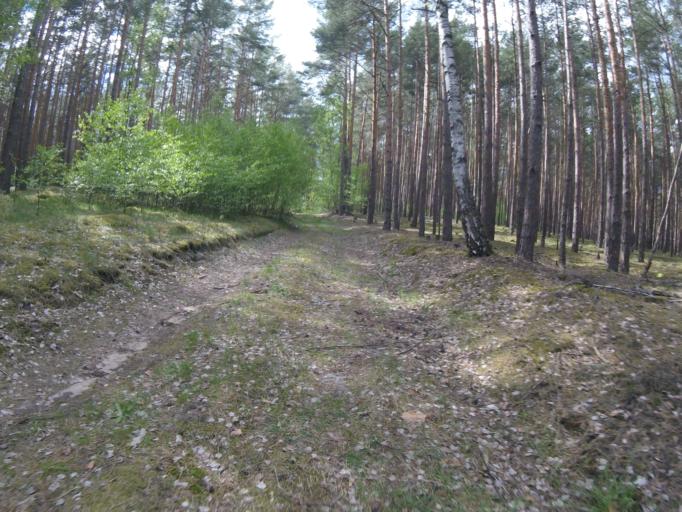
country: DE
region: Brandenburg
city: Teupitz
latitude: 52.1539
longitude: 13.6019
